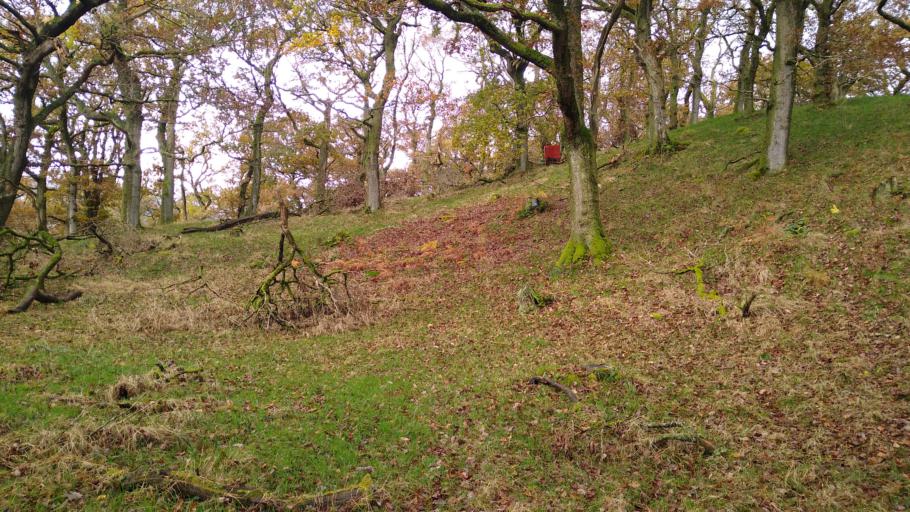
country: GB
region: England
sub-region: Cumbria
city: Keswick
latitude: 54.6478
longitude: -3.2312
